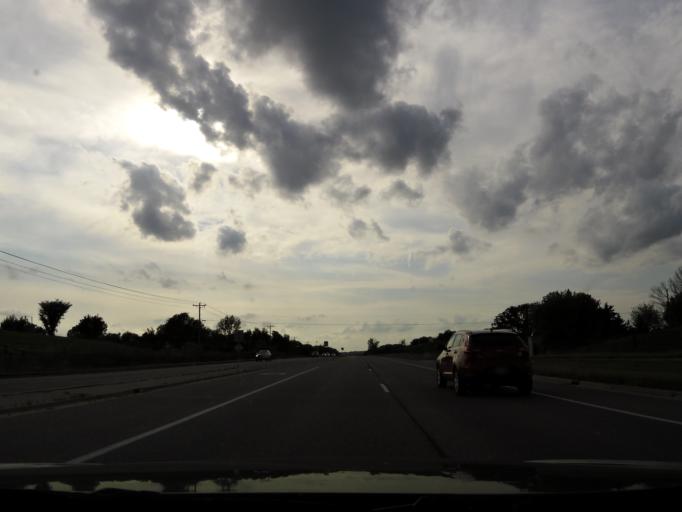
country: US
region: Minnesota
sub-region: Dakota County
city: Lakeville
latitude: 44.6814
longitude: -93.3313
